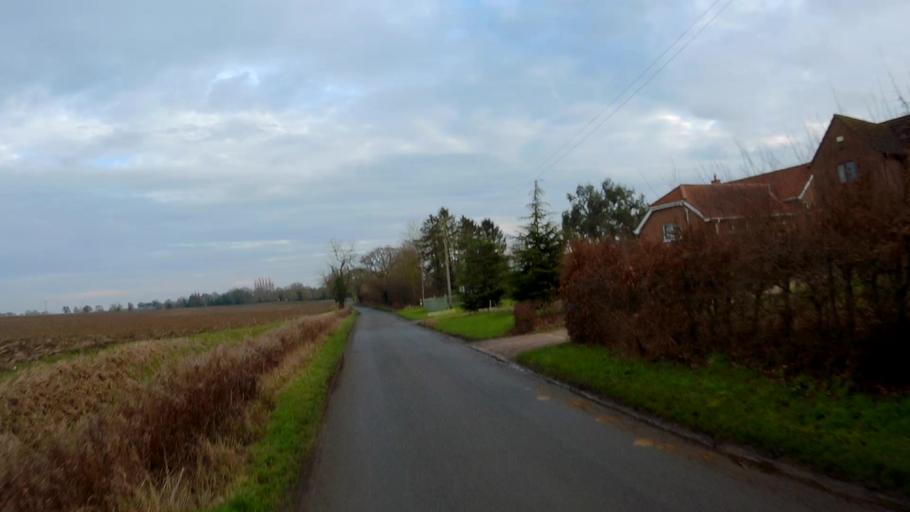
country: GB
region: England
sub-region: Lincolnshire
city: Bourne
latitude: 52.8314
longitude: -0.4206
